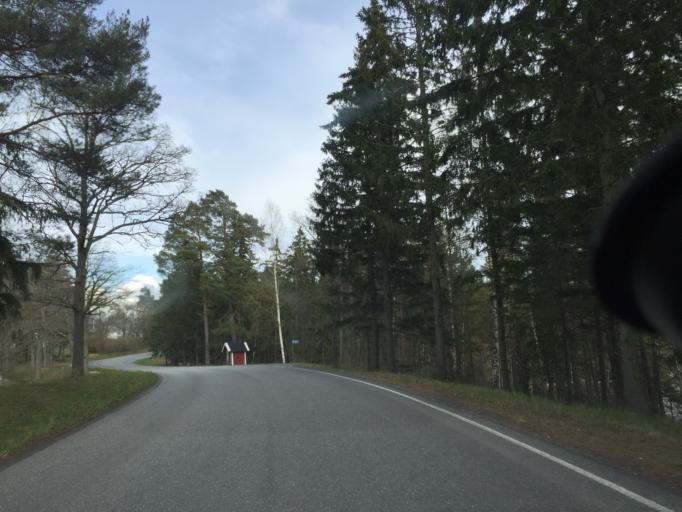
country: FI
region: Varsinais-Suomi
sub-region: Salo
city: Saerkisalo
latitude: 60.0056
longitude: 23.1038
